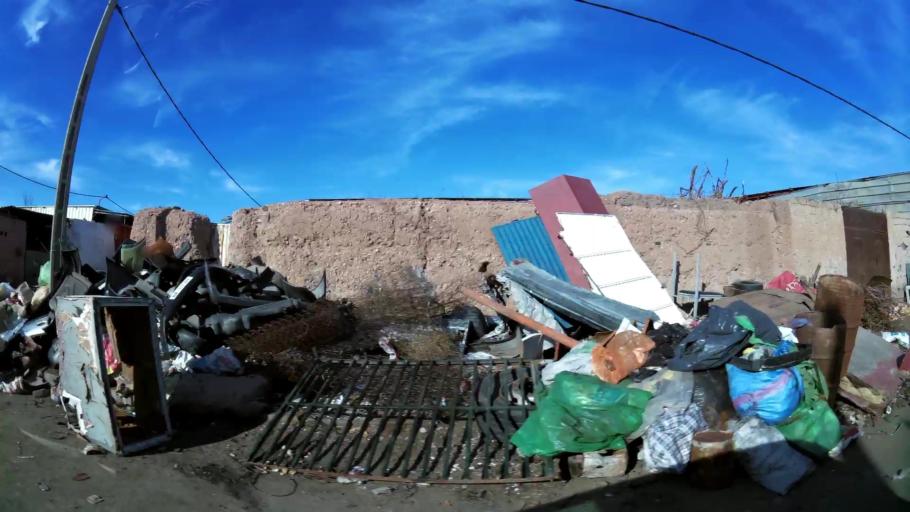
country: MA
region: Marrakech-Tensift-Al Haouz
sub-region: Marrakech
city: Marrakesh
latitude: 31.6829
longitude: -8.0558
